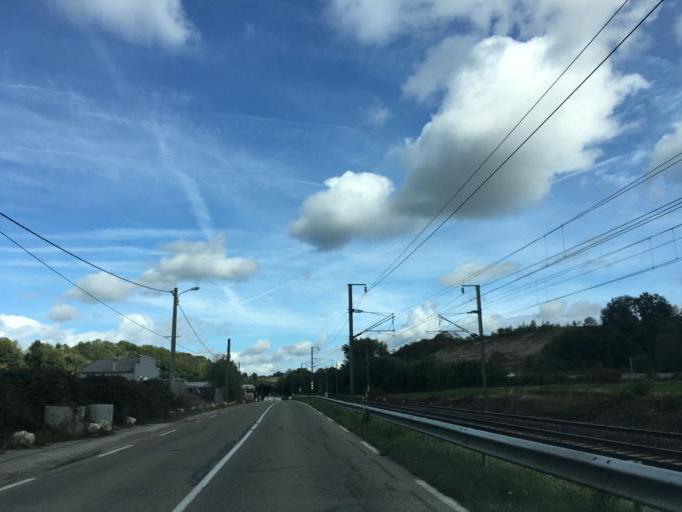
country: FR
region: Rhone-Alpes
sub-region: Departement de l'Isere
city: Saint-Didier-de-la-Tour
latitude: 45.5592
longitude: 5.4660
